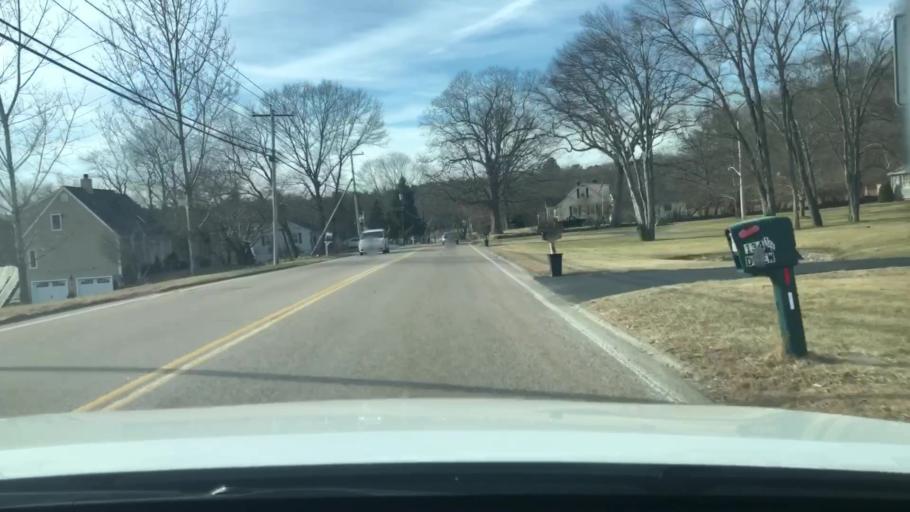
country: US
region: Massachusetts
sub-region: Worcester County
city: Grafton
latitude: 42.1980
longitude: -71.7180
